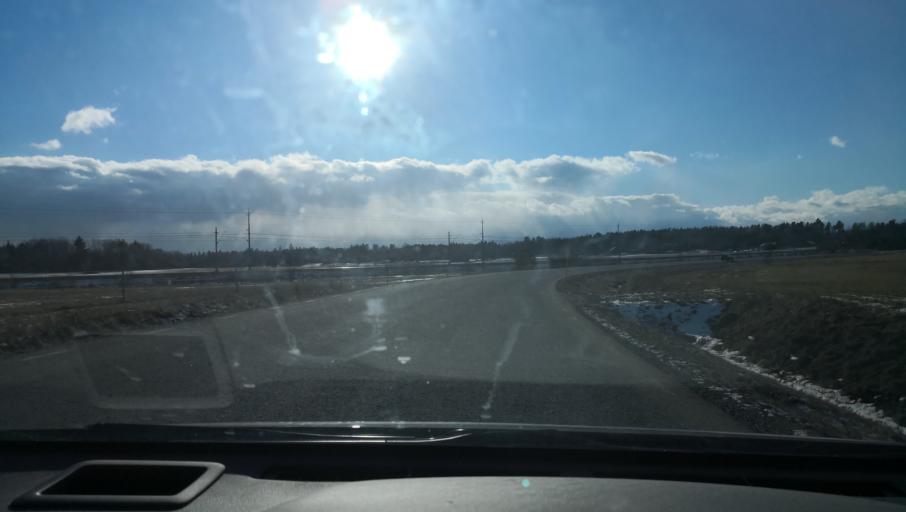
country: SE
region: Uppsala
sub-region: Enkopings Kommun
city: Hummelsta
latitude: 59.6536
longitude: 16.9545
